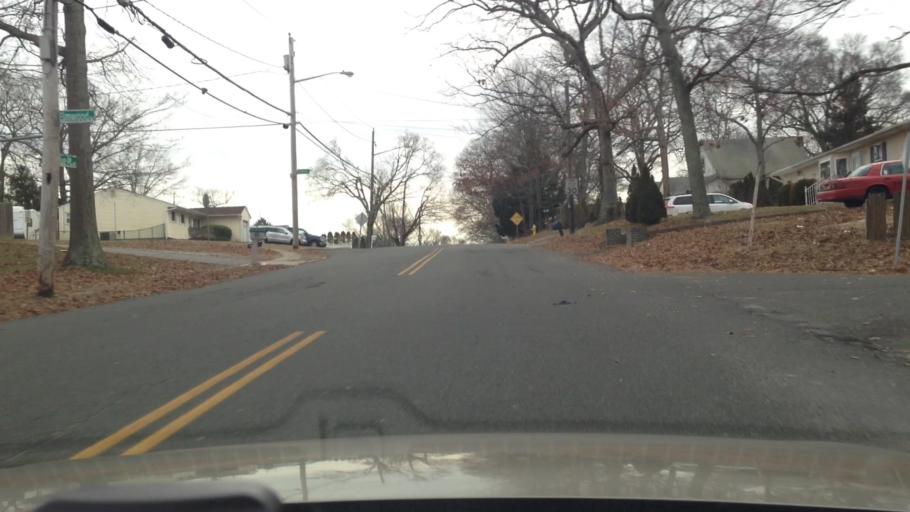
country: US
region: New York
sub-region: Suffolk County
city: Selden
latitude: 40.8627
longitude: -73.0348
